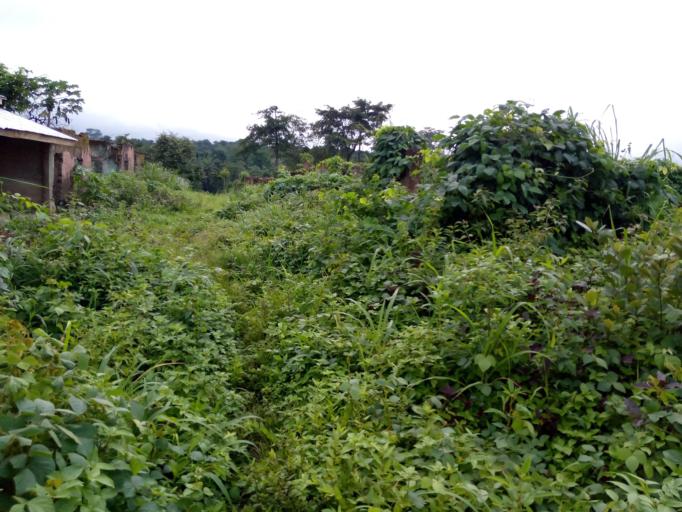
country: SL
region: Eastern Province
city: Buedu
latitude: 8.4656
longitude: -10.3388
